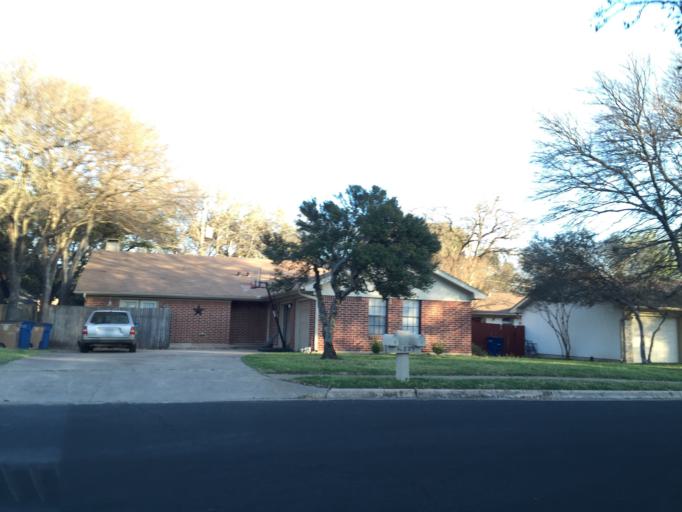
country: US
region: Texas
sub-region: Williamson County
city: Jollyville
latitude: 30.4272
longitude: -97.7634
